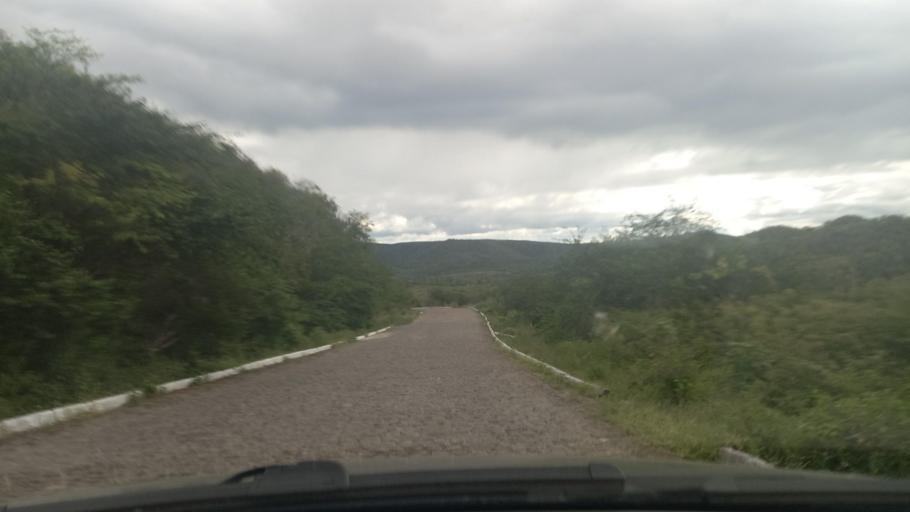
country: BR
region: Sergipe
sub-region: Caninde De Sao Francisco
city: Caninde de Sao Francisco
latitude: -9.6220
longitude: -37.8035
